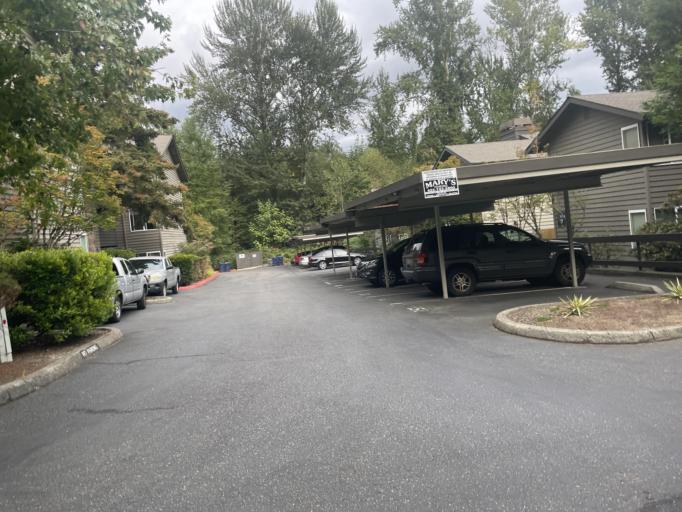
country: US
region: Washington
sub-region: King County
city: Inglewood-Finn Hill
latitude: 47.7068
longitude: -122.2169
